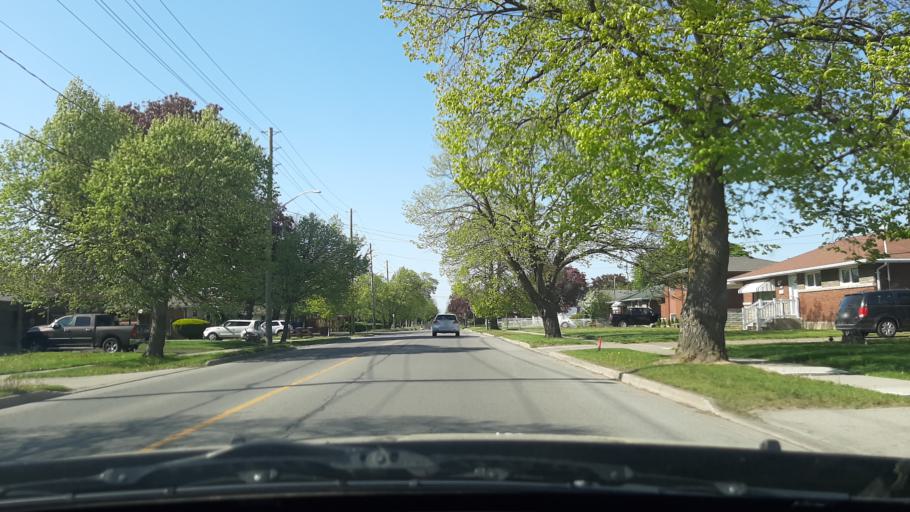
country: CA
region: Ontario
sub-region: Regional Municipality of Niagara
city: St. Catharines
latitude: 43.1900
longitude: -79.2109
